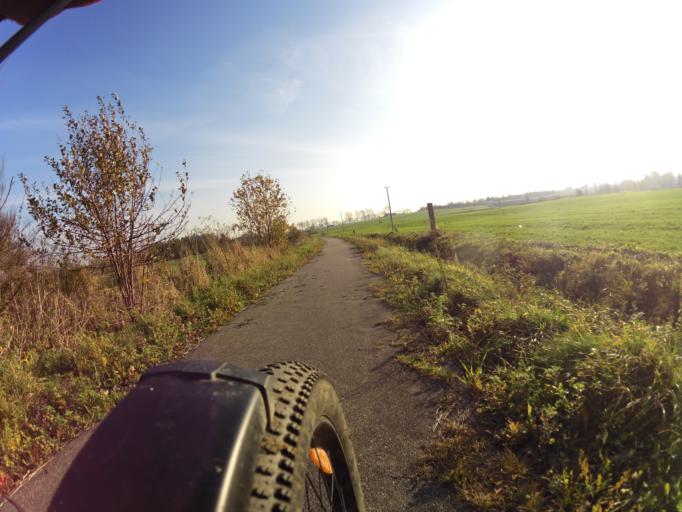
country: PL
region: Pomeranian Voivodeship
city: Strzelno
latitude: 54.7635
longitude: 18.2551
